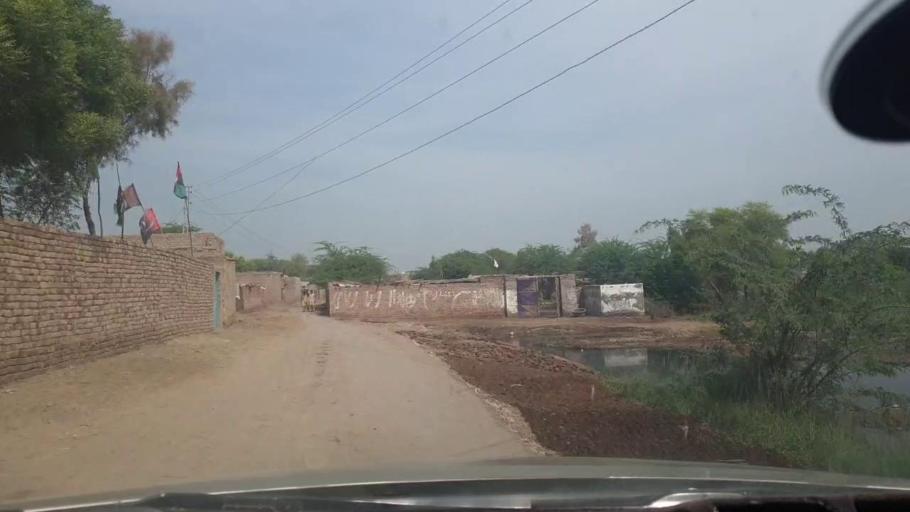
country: PK
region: Sindh
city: Jacobabad
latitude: 28.2964
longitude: 68.4777
